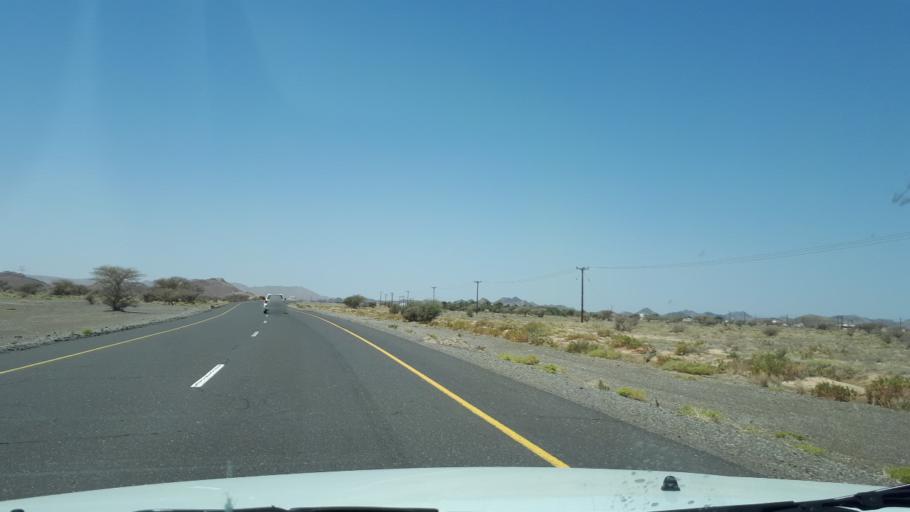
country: OM
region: Ash Sharqiyah
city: Ibra'
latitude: 22.6193
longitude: 58.4043
